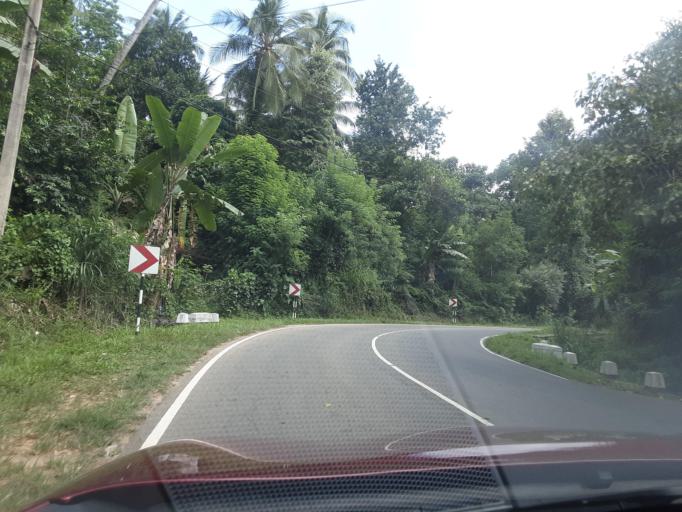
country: LK
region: Uva
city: Monaragala
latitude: 6.8977
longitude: 81.2497
